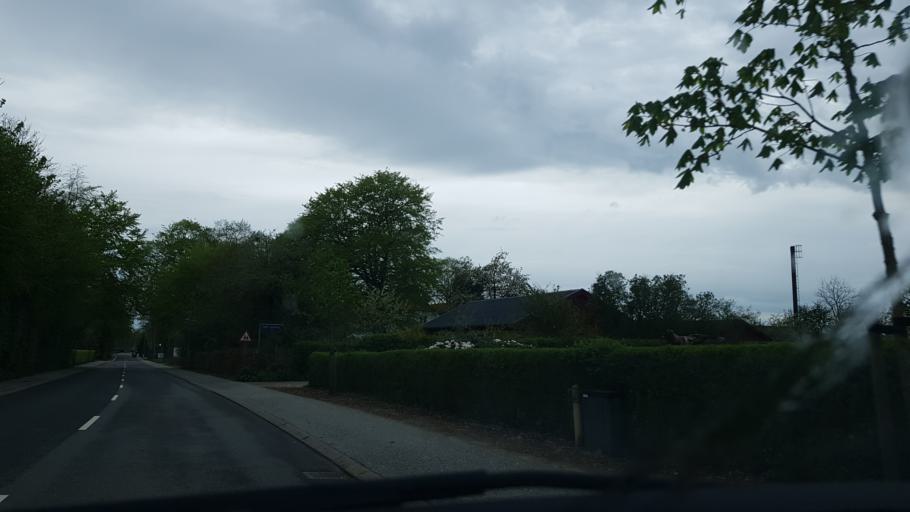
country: DK
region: South Denmark
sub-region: Kolding Kommune
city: Lunderskov
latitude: 55.4638
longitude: 9.3466
